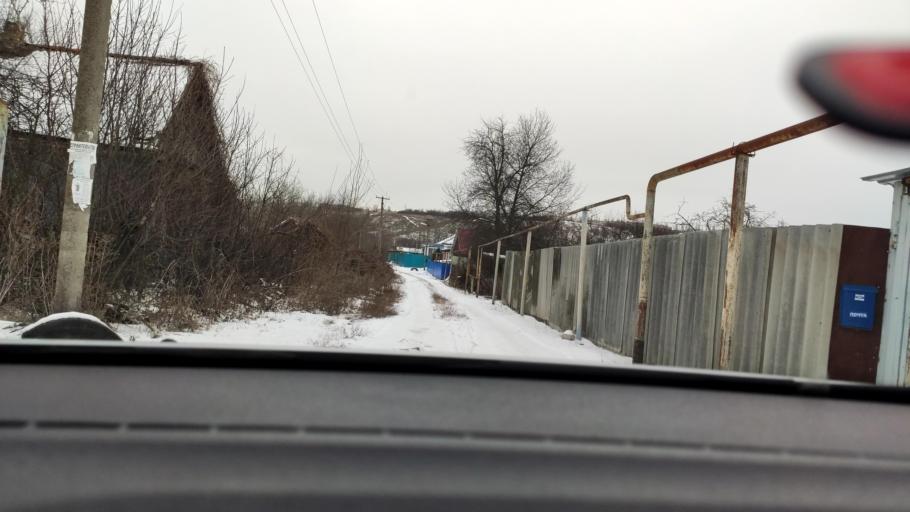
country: RU
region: Voronezj
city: Semiluki
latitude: 51.7014
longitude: 38.9990
